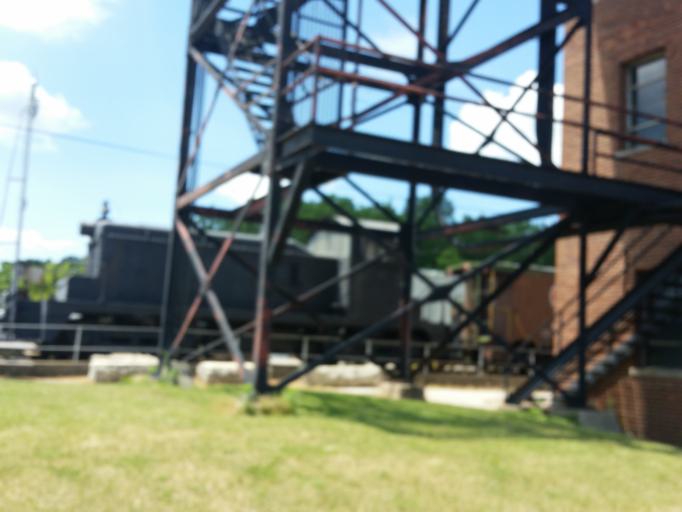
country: US
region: Iowa
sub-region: Fayette County
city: Oelwein
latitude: 42.6771
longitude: -91.9164
